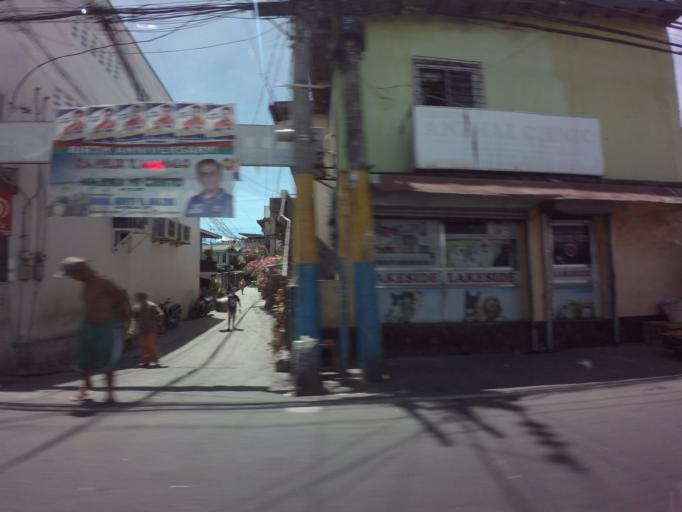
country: PH
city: Sambayanihan People's Village
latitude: 14.4543
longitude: 121.0524
